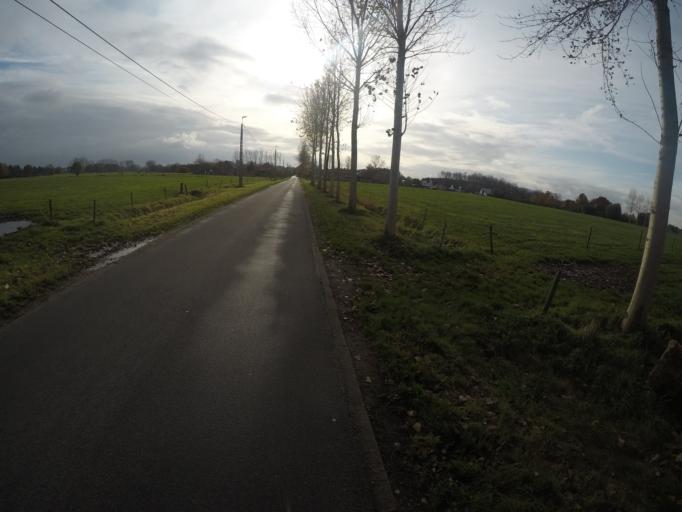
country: BE
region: Flanders
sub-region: Provincie Oost-Vlaanderen
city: Temse
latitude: 51.1624
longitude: 4.1901
